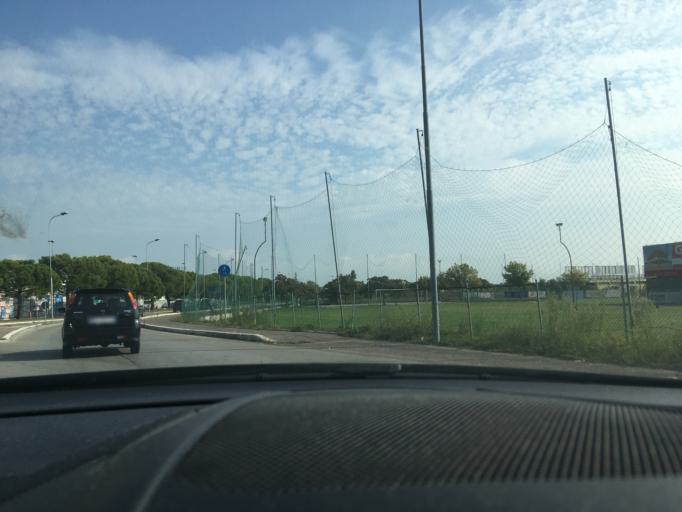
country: IT
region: Emilia-Romagna
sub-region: Forli-Cesena
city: San Mauro a Mare
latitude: 44.1557
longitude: 12.4341
